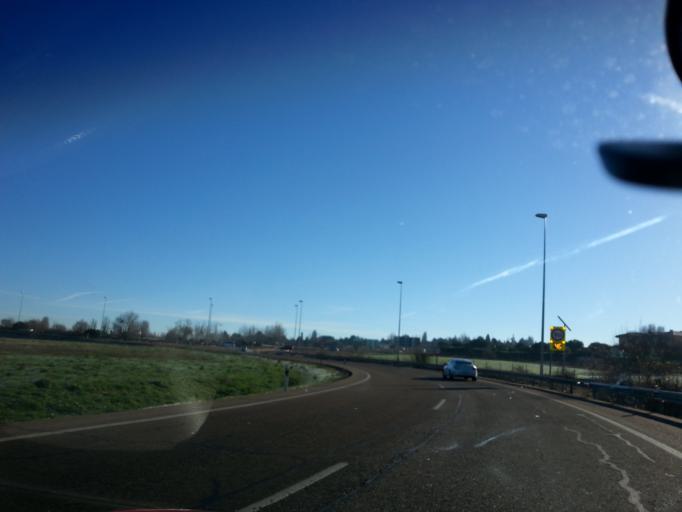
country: ES
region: Castille and Leon
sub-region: Provincia de Salamanca
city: Carbajosa de la Sagrada
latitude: 40.9421
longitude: -5.6410
